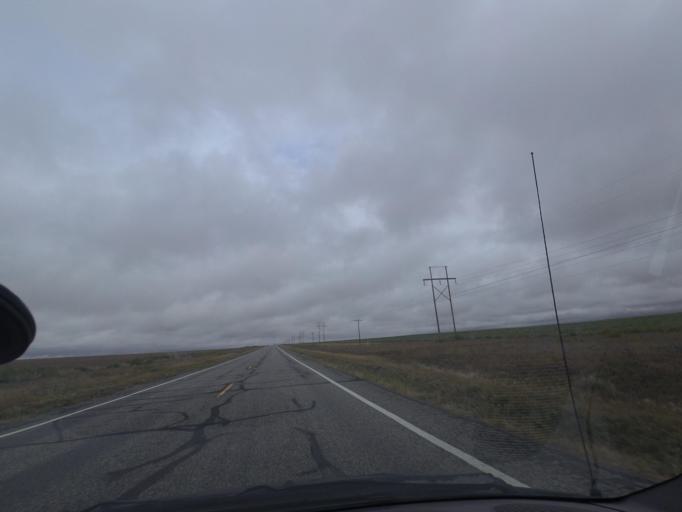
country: US
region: Colorado
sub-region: Washington County
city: Akron
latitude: 39.7399
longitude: -103.3020
